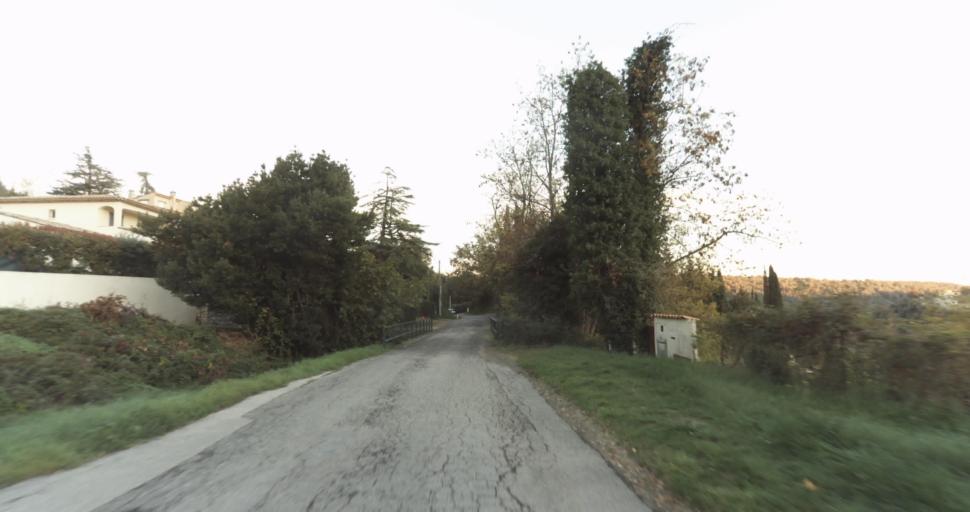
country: FR
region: Provence-Alpes-Cote d'Azur
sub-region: Departement des Alpes-Maritimes
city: Saint-Jeannet
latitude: 43.7364
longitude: 7.1293
